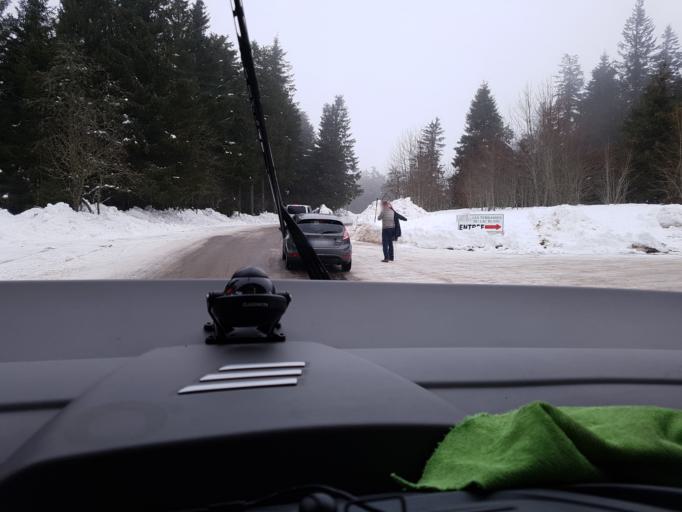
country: FR
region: Alsace
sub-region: Departement du Haut-Rhin
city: Soultzeren
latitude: 48.1353
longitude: 7.0897
